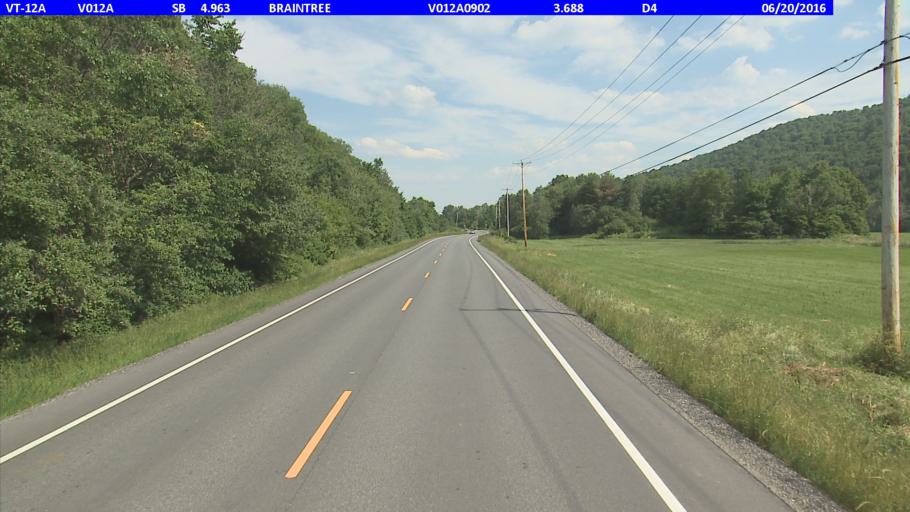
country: US
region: Vermont
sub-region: Orange County
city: Randolph
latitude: 43.9633
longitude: -72.7389
